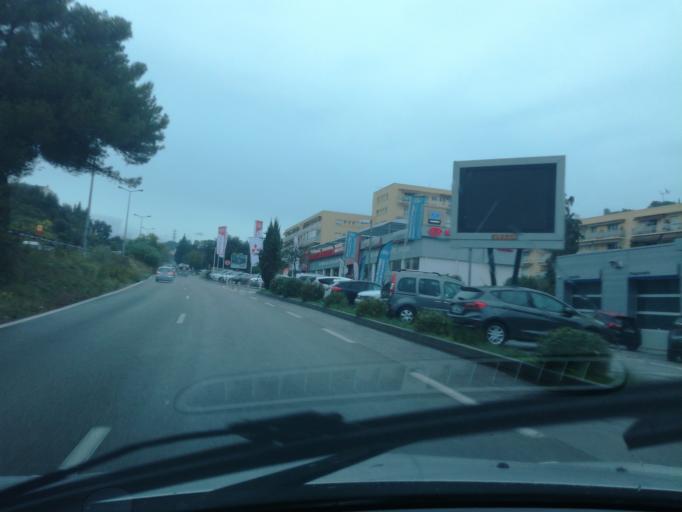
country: FR
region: Provence-Alpes-Cote d'Azur
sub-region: Departement des Alpes-Maritimes
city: Le Cannet
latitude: 43.5780
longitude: 7.0121
